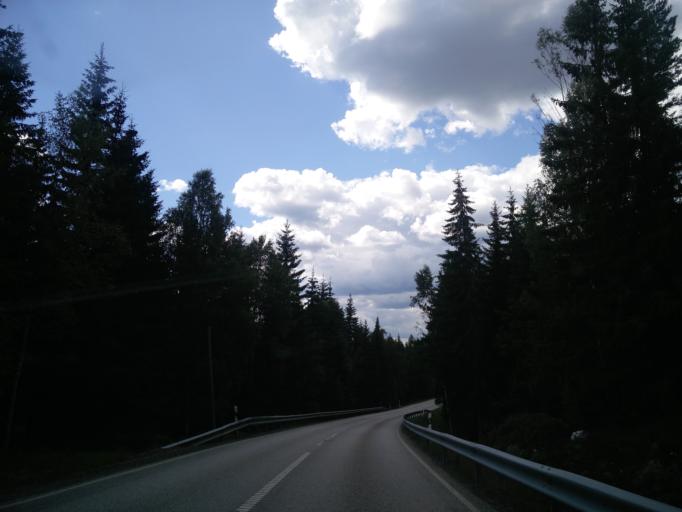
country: SE
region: OErebro
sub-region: Hallefors Kommun
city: Haellefors
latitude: 59.7913
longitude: 14.7524
